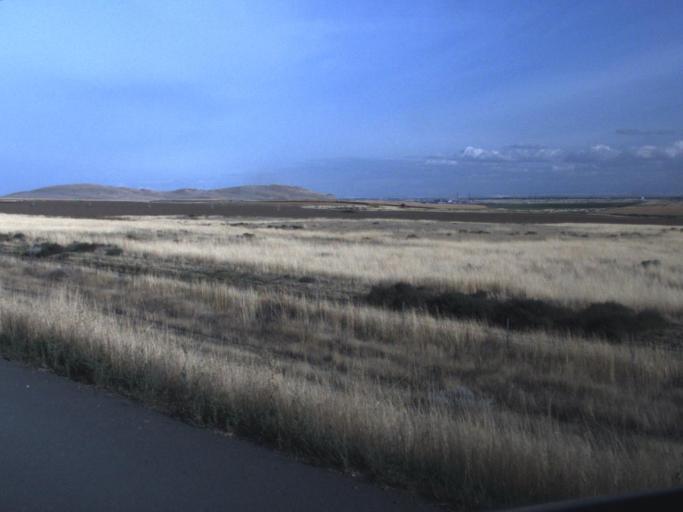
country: US
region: Oregon
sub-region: Umatilla County
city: Umatilla
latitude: 45.9552
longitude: -119.4196
